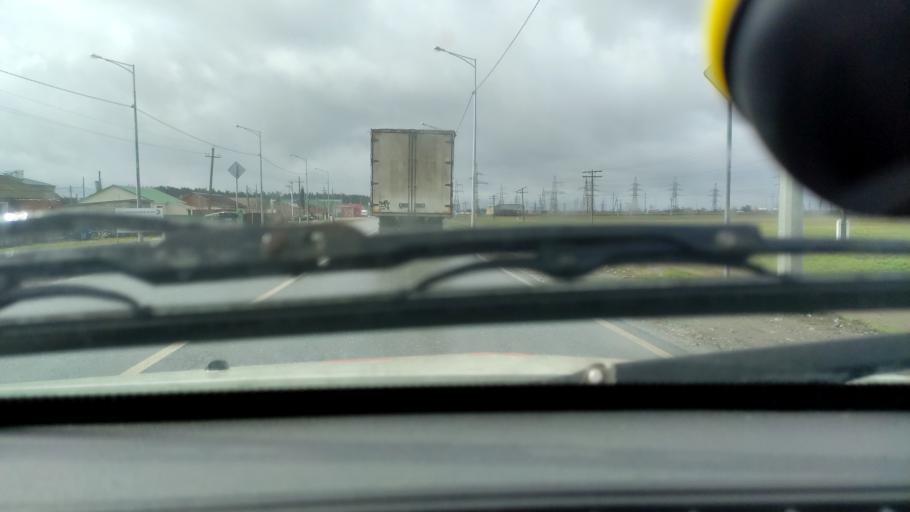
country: RU
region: Samara
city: Zhigulevsk
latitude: 53.5460
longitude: 49.5192
